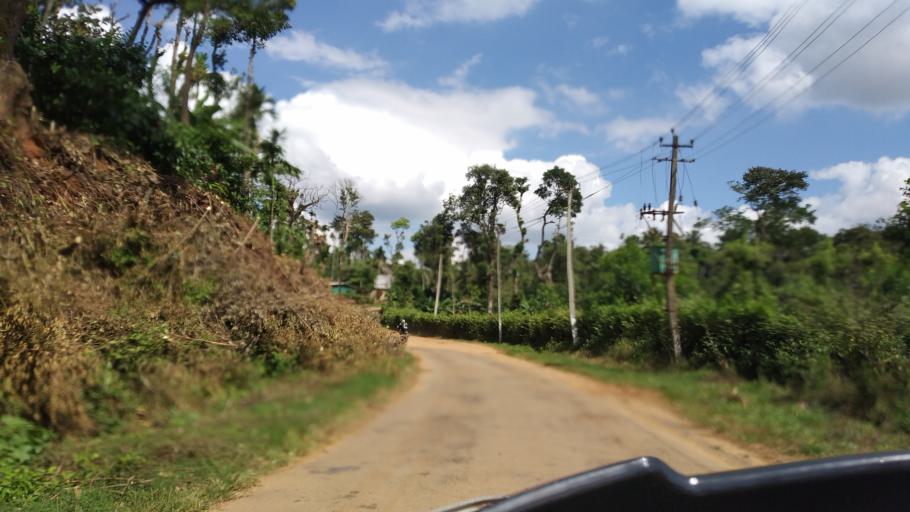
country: IN
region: Karnataka
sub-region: Kodagu
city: Ponnampet
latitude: 12.0303
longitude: 75.8970
